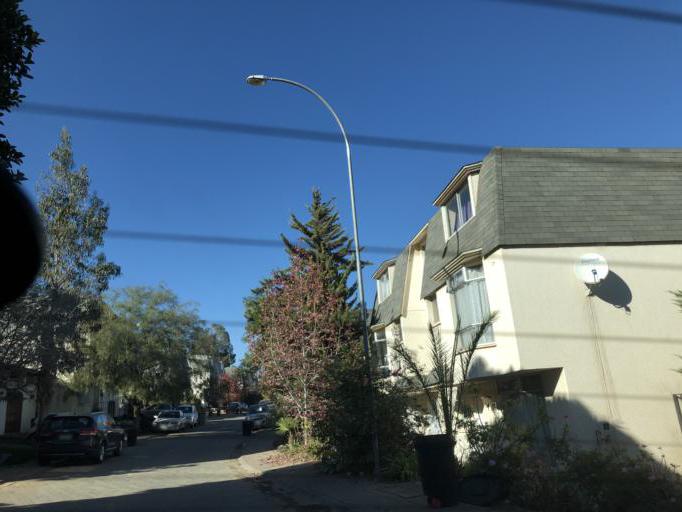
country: CL
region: Santiago Metropolitan
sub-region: Provincia de Cordillera
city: Puente Alto
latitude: -33.5556
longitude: -70.5331
